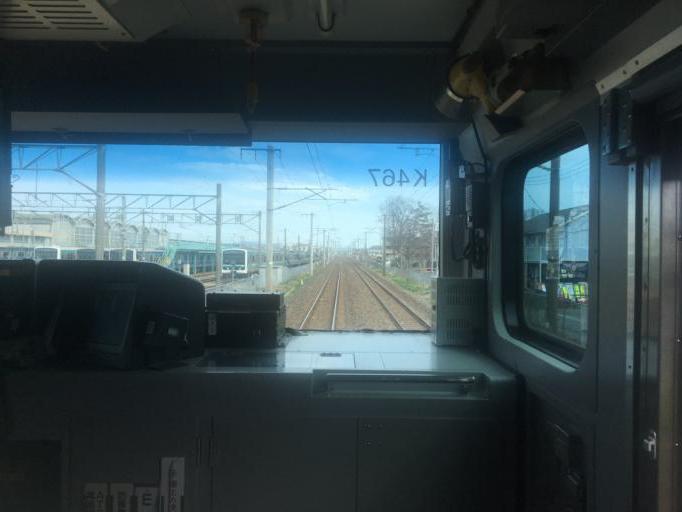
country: JP
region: Ibaraki
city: Hitachi-Naka
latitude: 36.4050
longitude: 140.5281
